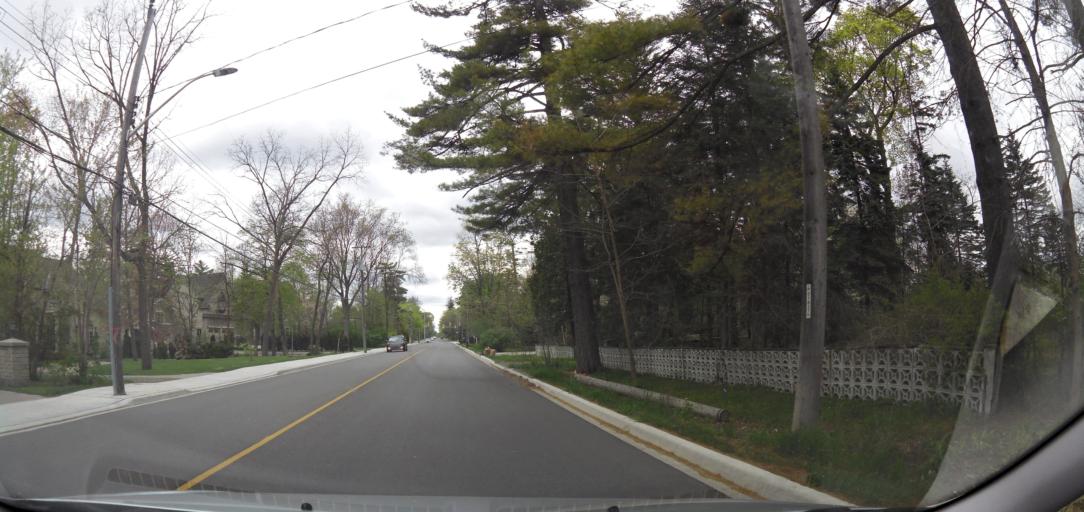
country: CA
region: Ontario
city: Mississauga
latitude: 43.5509
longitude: -79.5997
